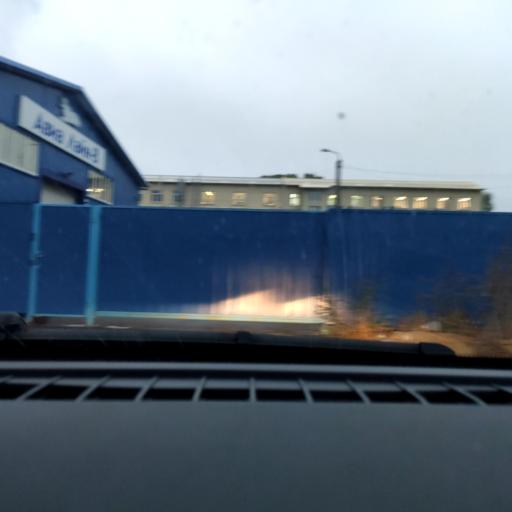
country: RU
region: Voronezj
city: Voronezh
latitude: 51.6320
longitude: 39.2435
